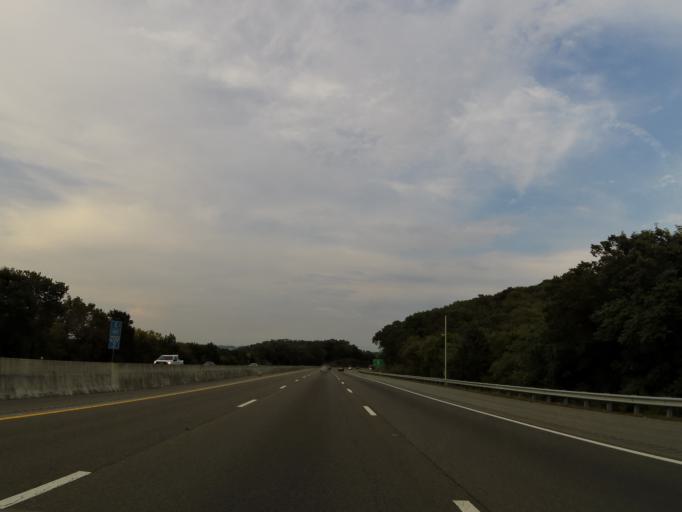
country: US
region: Tennessee
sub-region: Davidson County
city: Belle Meade
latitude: 36.1215
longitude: -86.9104
